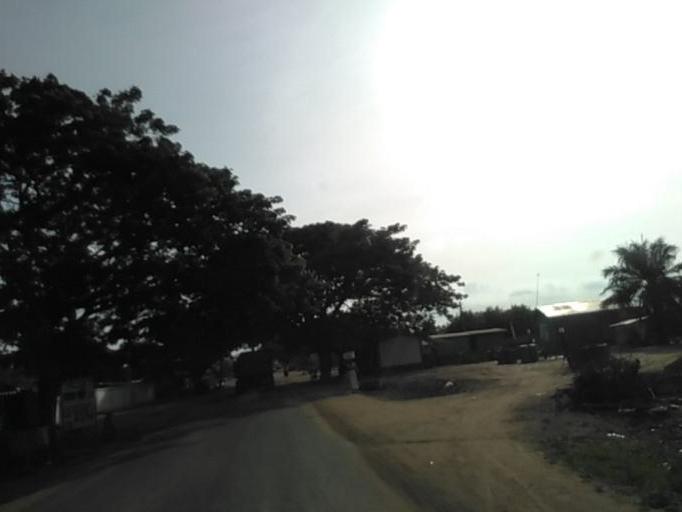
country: GH
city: Akropong
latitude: 6.0972
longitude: 0.1221
